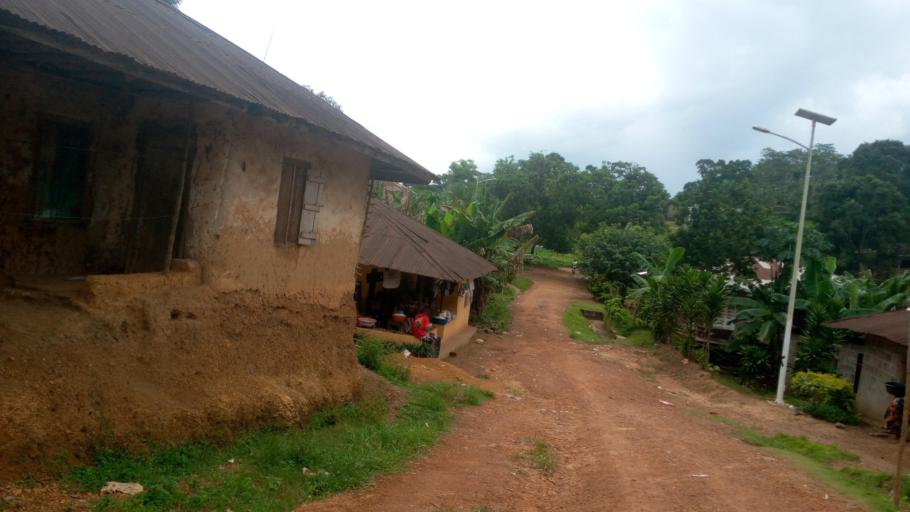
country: SL
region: Southern Province
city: Mogbwemo
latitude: 7.6048
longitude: -12.1766
